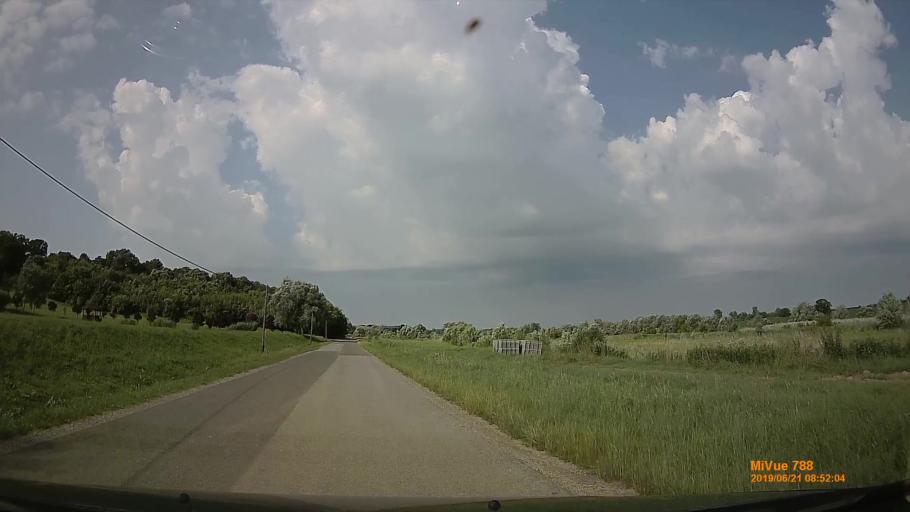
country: HU
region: Baranya
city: Buekkoesd
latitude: 46.1713
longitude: 17.9028
